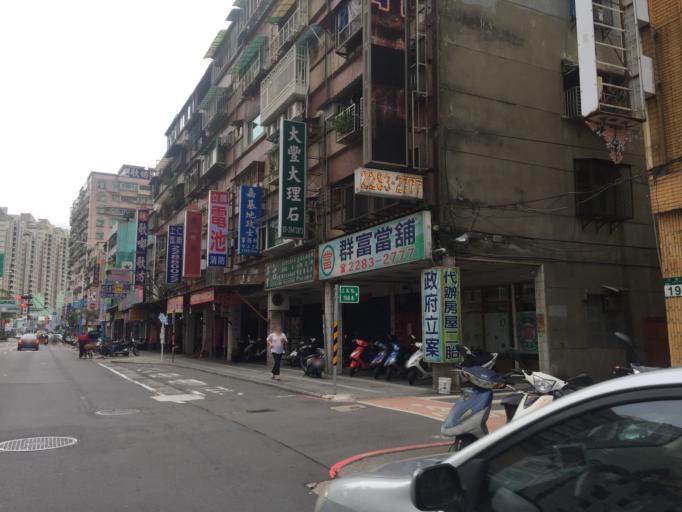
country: TW
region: Taipei
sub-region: Taipei
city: Banqiao
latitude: 25.0888
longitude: 121.4693
